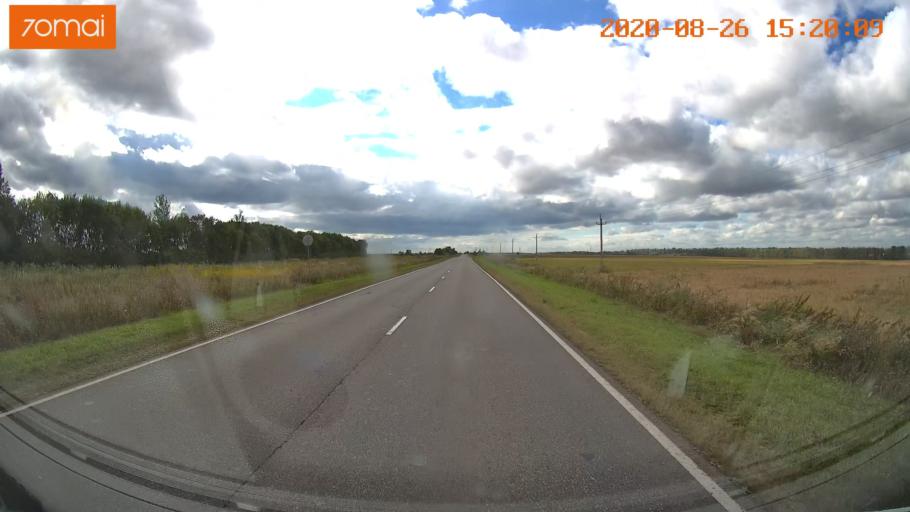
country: RU
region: Tula
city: Severo-Zadonsk
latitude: 54.1423
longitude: 38.5041
